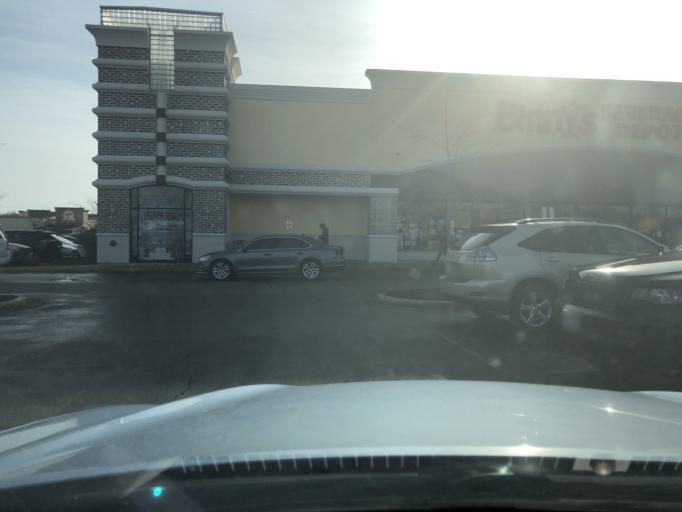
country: US
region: Illinois
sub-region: Cook County
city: Hoffman Estates
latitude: 42.0481
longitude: -88.0869
